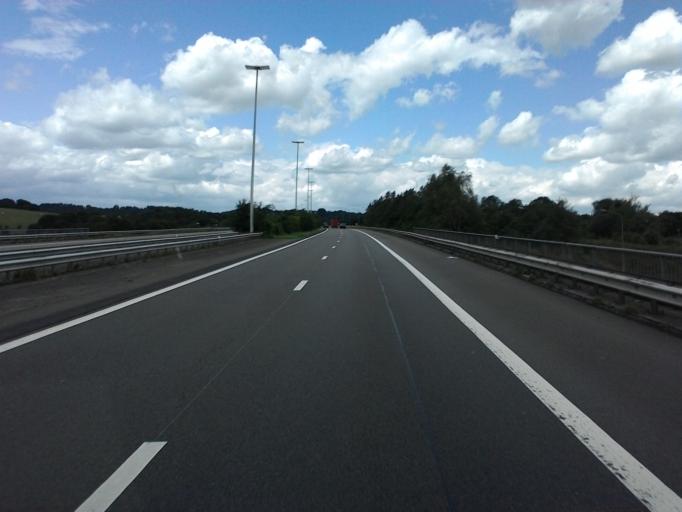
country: BE
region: Wallonia
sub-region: Province de Liege
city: Aywaille
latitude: 50.4894
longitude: 5.7132
